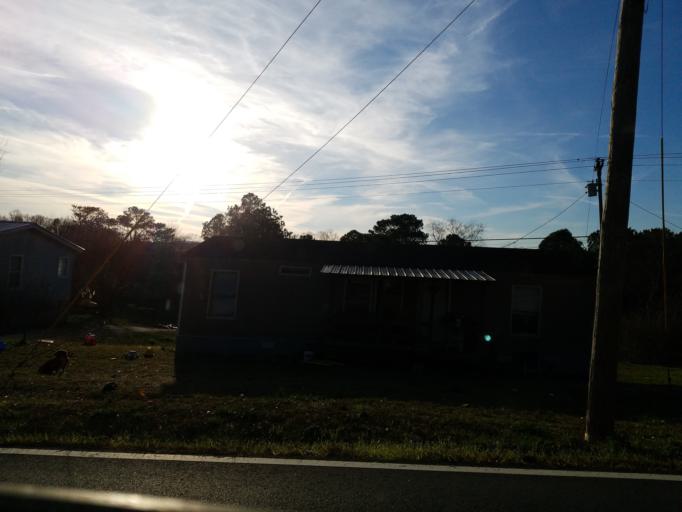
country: US
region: Georgia
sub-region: Gordon County
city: Calhoun
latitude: 34.5595
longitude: -84.9710
